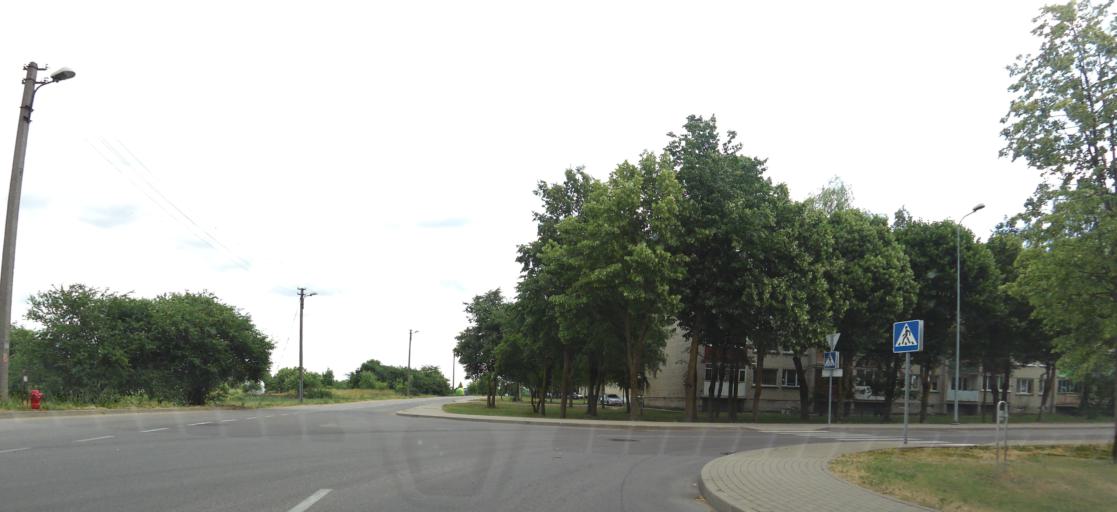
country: LT
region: Vilnius County
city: Ukmerge
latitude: 55.2611
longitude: 24.7783
